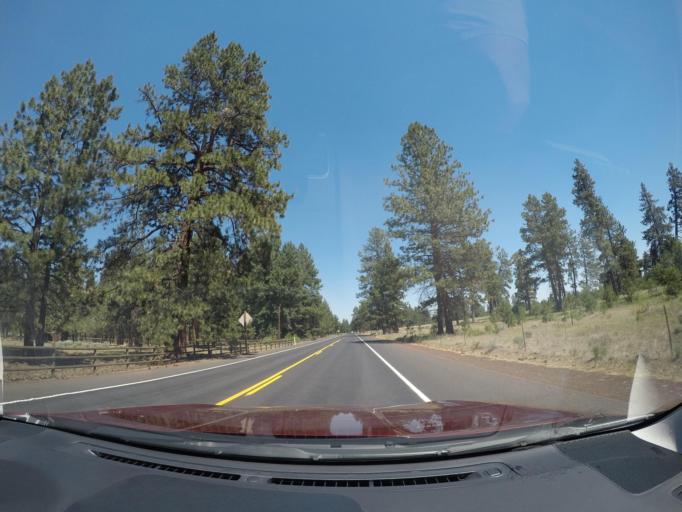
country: US
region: Oregon
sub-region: Deschutes County
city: Sisters
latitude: 44.2877
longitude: -121.5310
